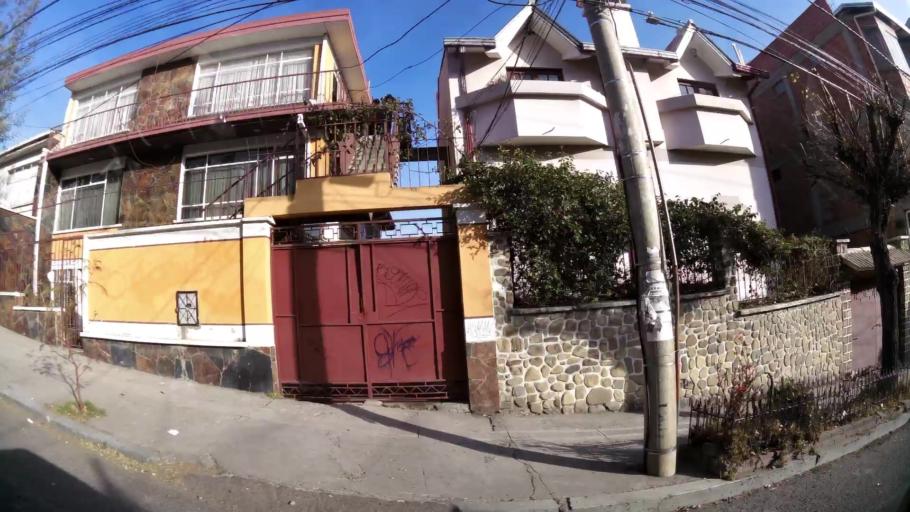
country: BO
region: La Paz
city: La Paz
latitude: -16.5259
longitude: -68.1056
